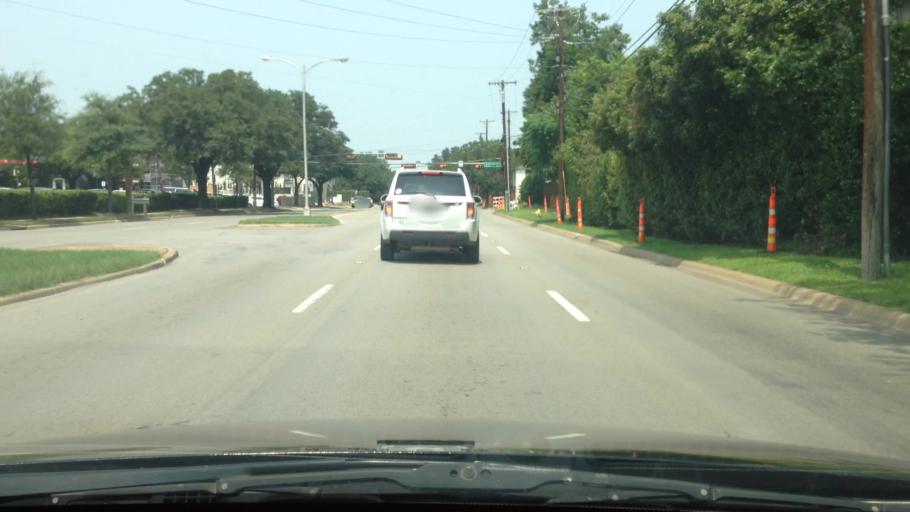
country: US
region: Texas
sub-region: Dallas County
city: University Park
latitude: 32.8438
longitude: -96.8214
